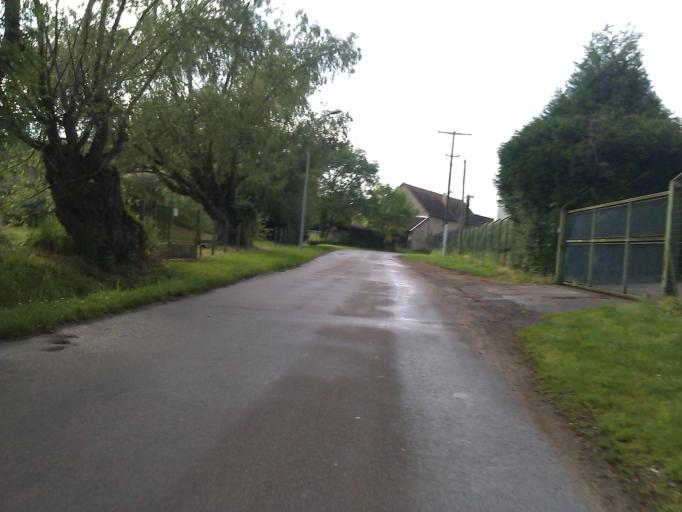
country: FR
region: Bourgogne
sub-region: Departement de Saone-et-Loire
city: Crissey
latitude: 46.8133
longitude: 4.8844
